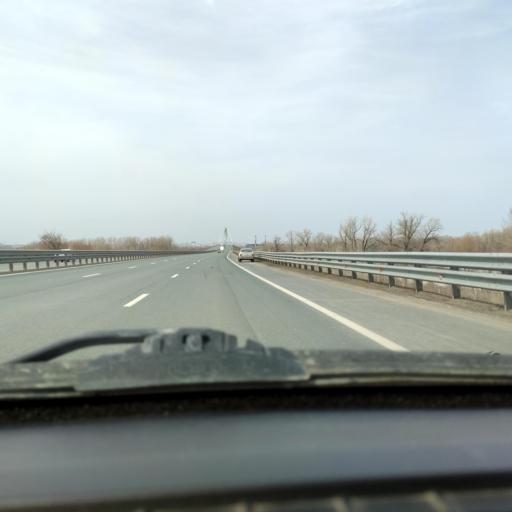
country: RU
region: Samara
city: Smyshlyayevka
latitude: 53.1685
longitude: 50.3170
